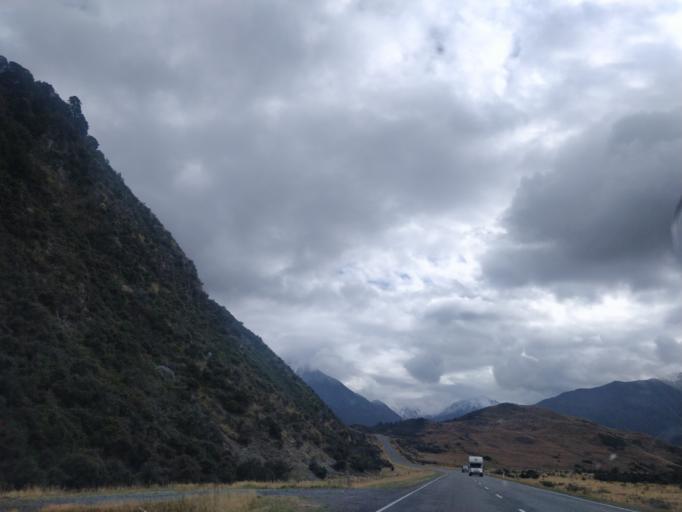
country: NZ
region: Canterbury
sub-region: Waimakariri District
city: Oxford
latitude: -43.0247
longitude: 171.7476
